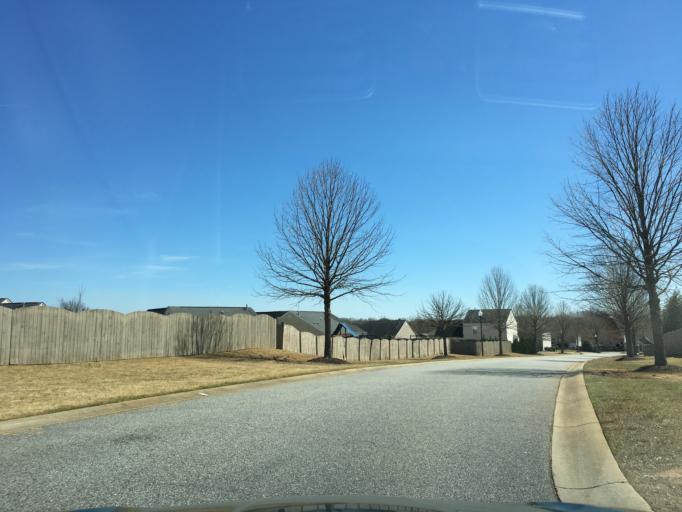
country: US
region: South Carolina
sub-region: Spartanburg County
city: Duncan
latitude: 34.8665
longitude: -82.1004
